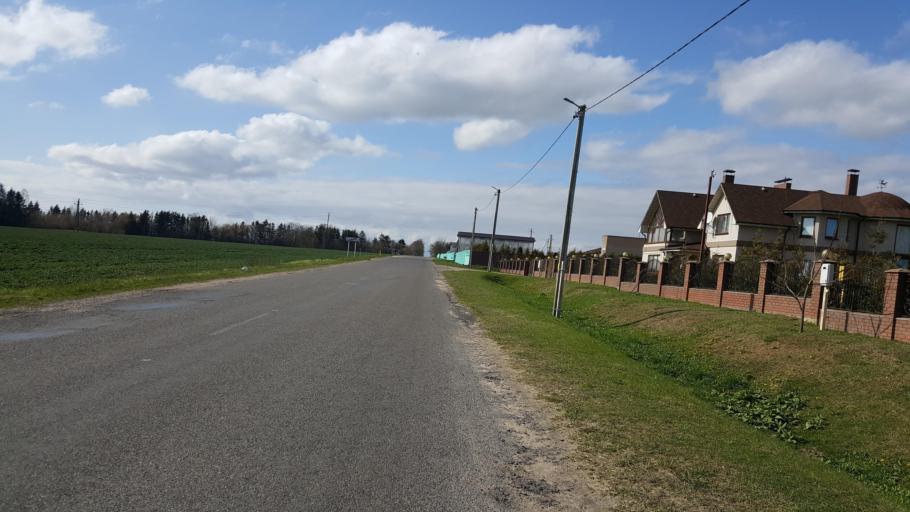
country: BY
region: Brest
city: Kamyanyets
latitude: 52.4084
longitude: 23.7945
